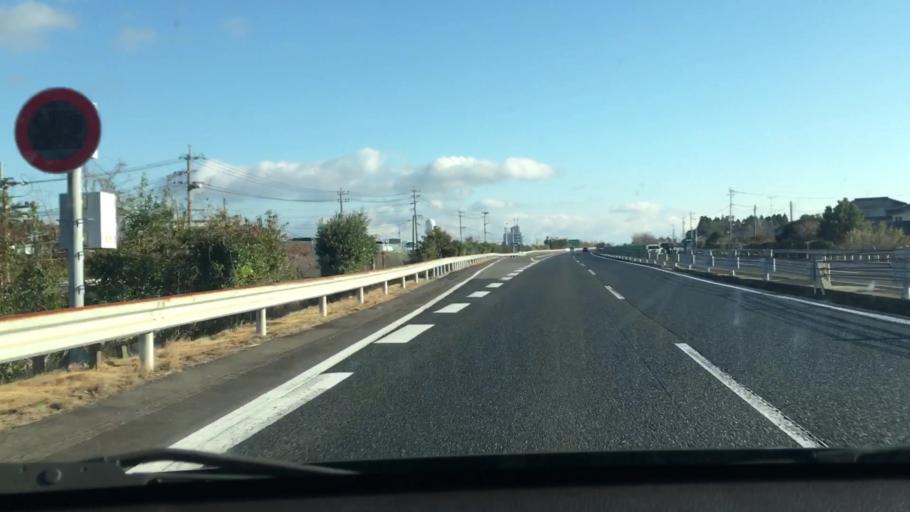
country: JP
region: Kagoshima
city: Kajiki
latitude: 31.8019
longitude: 130.7118
